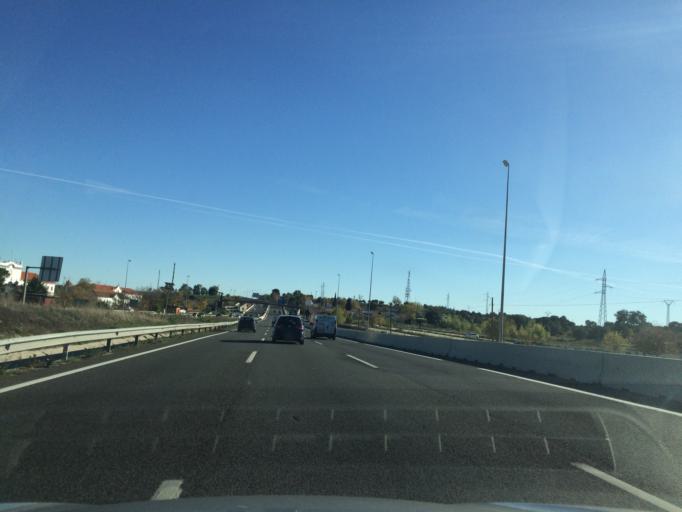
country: ES
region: Madrid
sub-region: Provincia de Madrid
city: Tres Cantos
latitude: 40.5585
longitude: -3.7124
